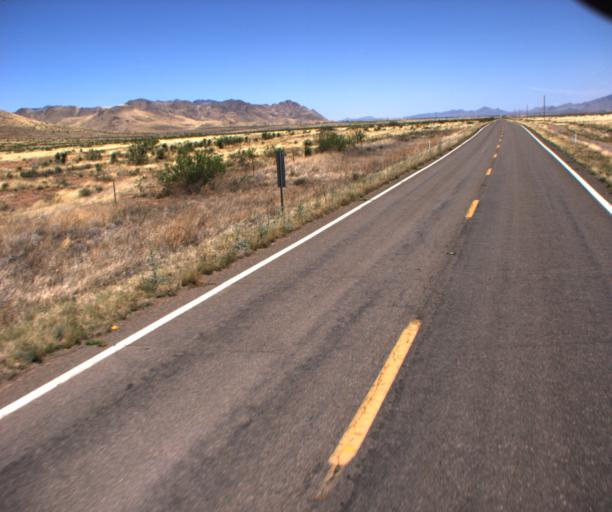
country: US
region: Arizona
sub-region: Cochise County
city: Douglas
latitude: 31.6564
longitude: -109.1565
